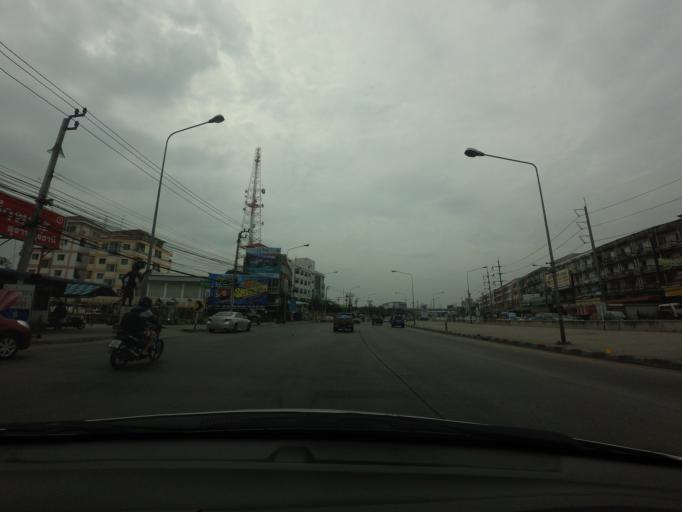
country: TH
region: Samut Prakan
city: Samut Prakan
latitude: 13.5972
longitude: 100.6117
